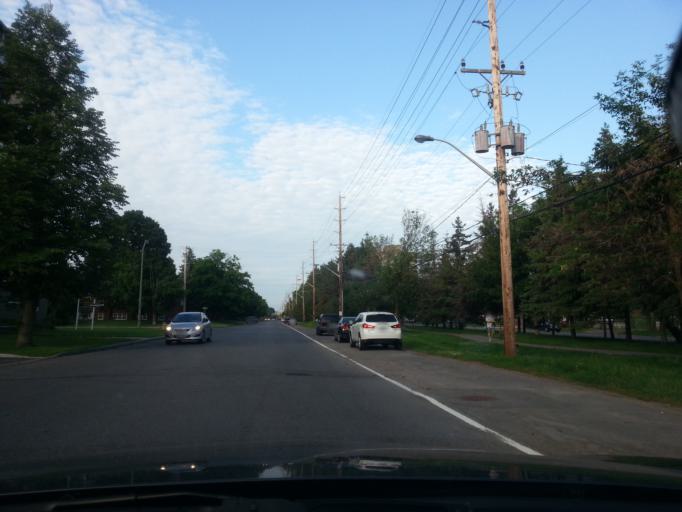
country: CA
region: Ontario
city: Ottawa
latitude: 45.3817
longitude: -75.7703
